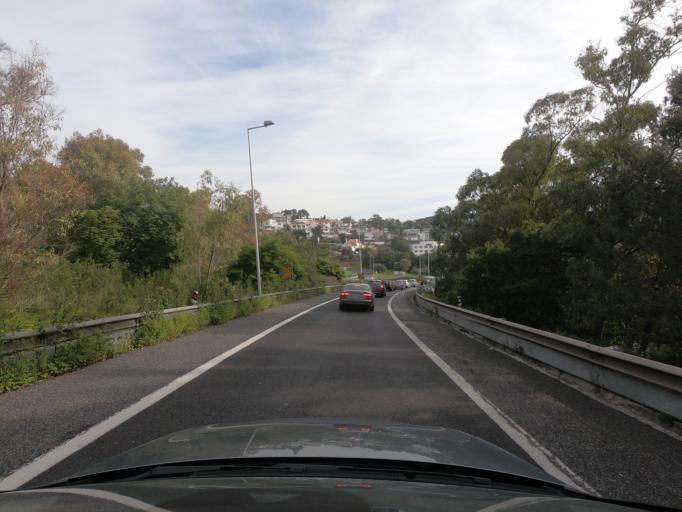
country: PT
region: Lisbon
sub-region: Oeiras
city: Quejas
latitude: 38.7126
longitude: -9.2616
